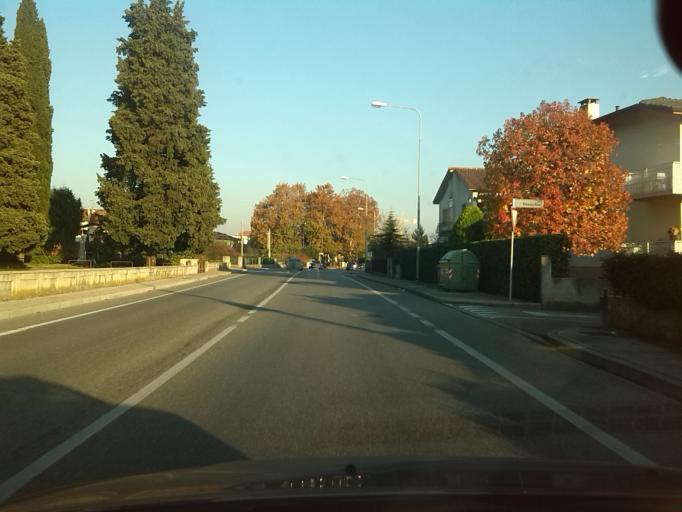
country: IT
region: Friuli Venezia Giulia
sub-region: Provincia di Udine
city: Udine
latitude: 46.0757
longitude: 13.2766
